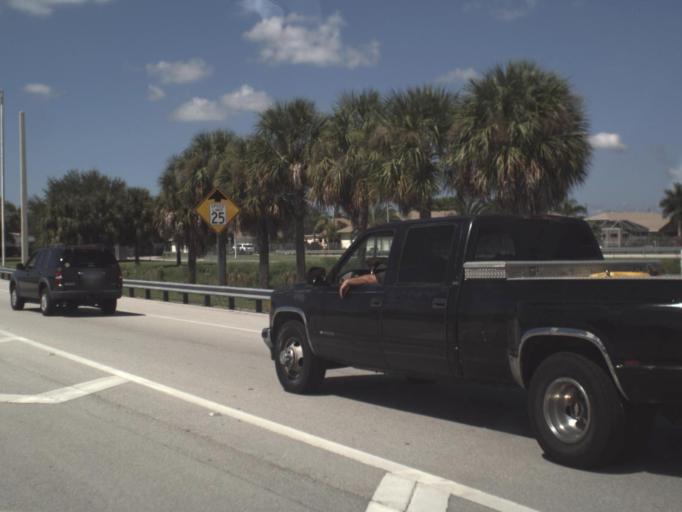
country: US
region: Florida
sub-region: Lee County
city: Lochmoor Waterway Estates
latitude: 26.6078
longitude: -81.9301
